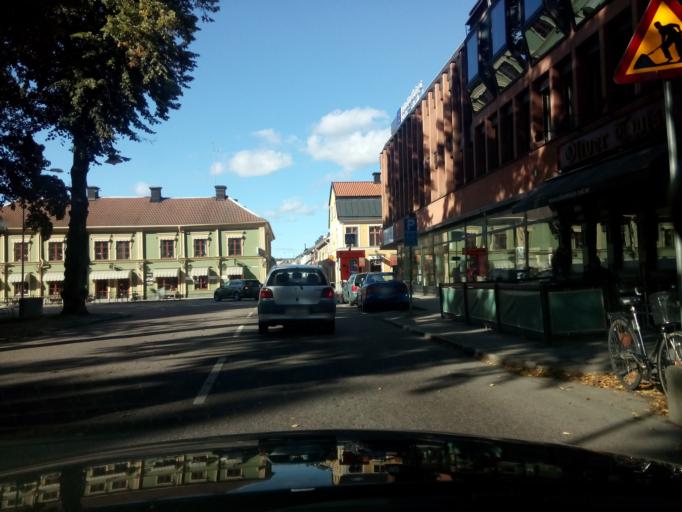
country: SE
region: Soedermanland
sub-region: Nykopings Kommun
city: Nykoping
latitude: 58.7509
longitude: 17.0025
